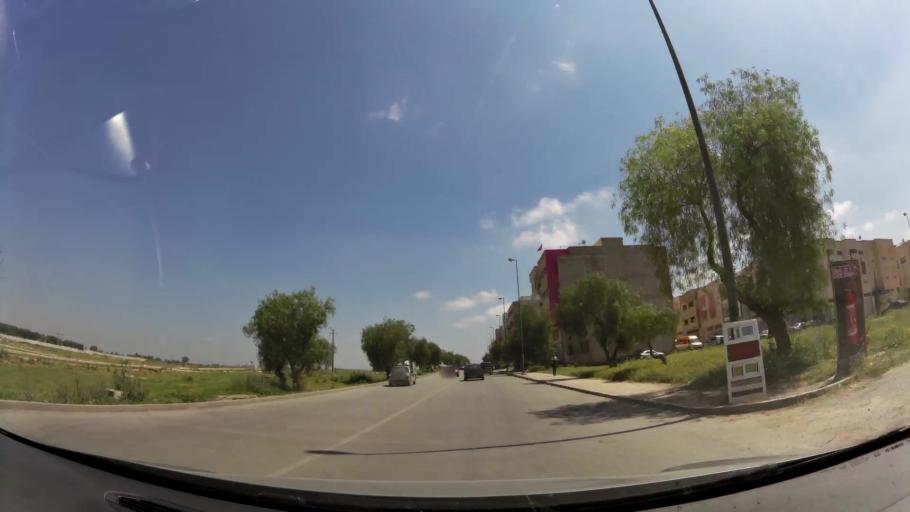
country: MA
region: Fes-Boulemane
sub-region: Fes
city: Fes
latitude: 34.0051
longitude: -5.0448
